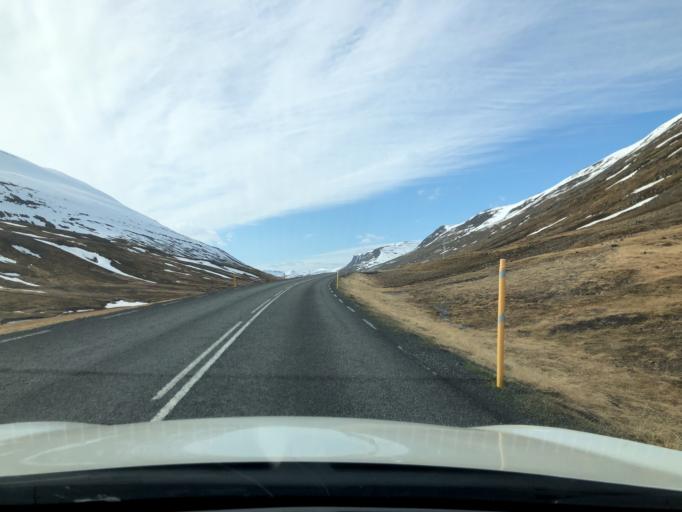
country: IS
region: East
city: Egilsstadir
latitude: 65.1702
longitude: -14.3382
